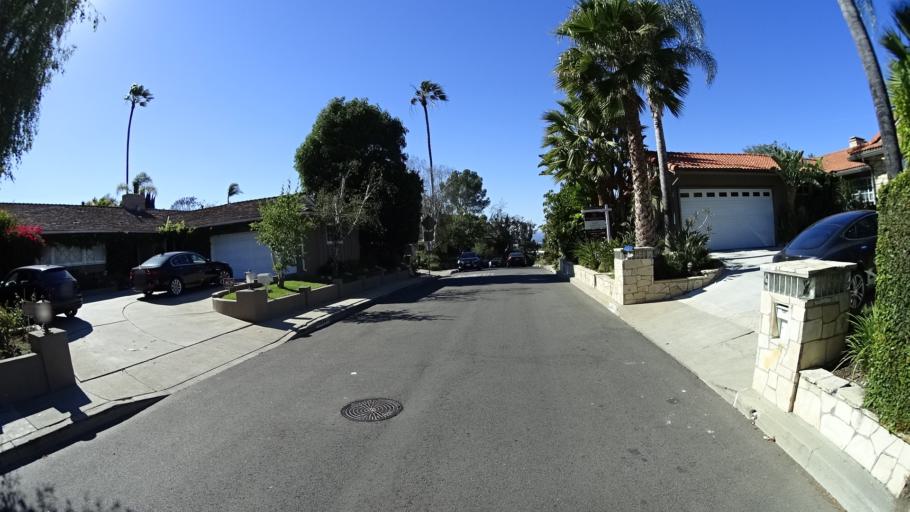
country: US
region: California
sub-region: Los Angeles County
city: Sherman Oaks
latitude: 34.1355
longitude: -118.4636
